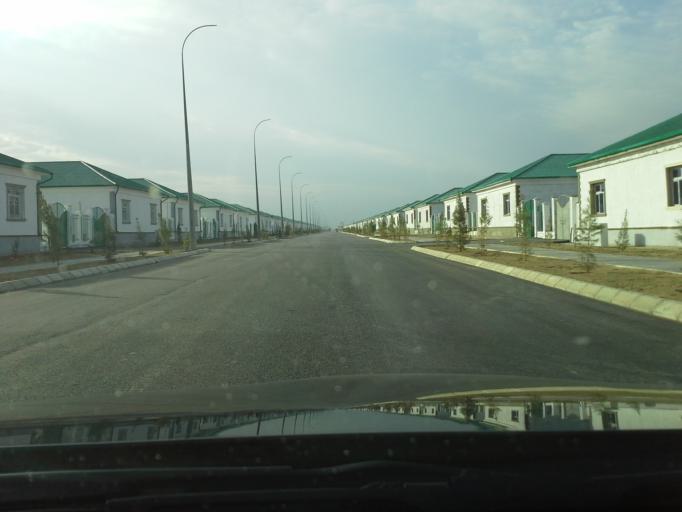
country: TM
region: Ahal
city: Abadan
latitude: 38.0968
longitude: 58.3063
